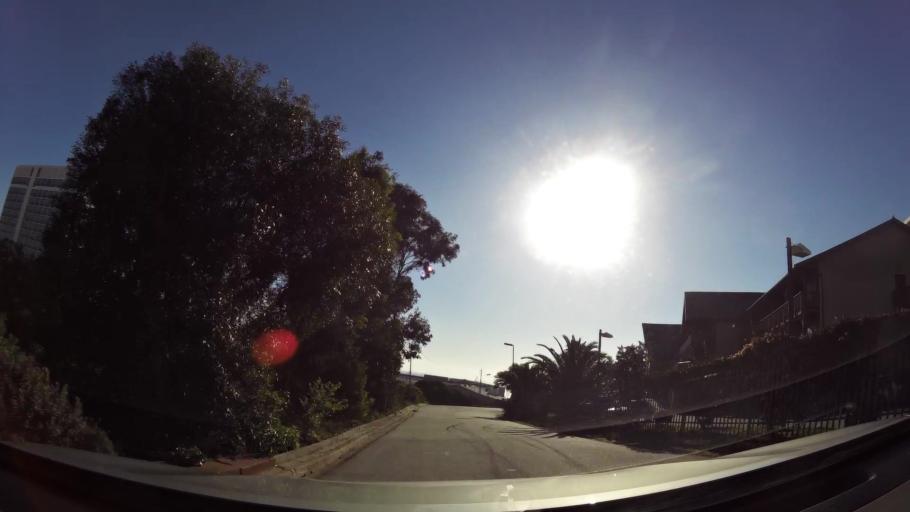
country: ZA
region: Eastern Cape
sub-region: Nelson Mandela Bay Metropolitan Municipality
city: Port Elizabeth
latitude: -33.9791
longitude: 25.6475
